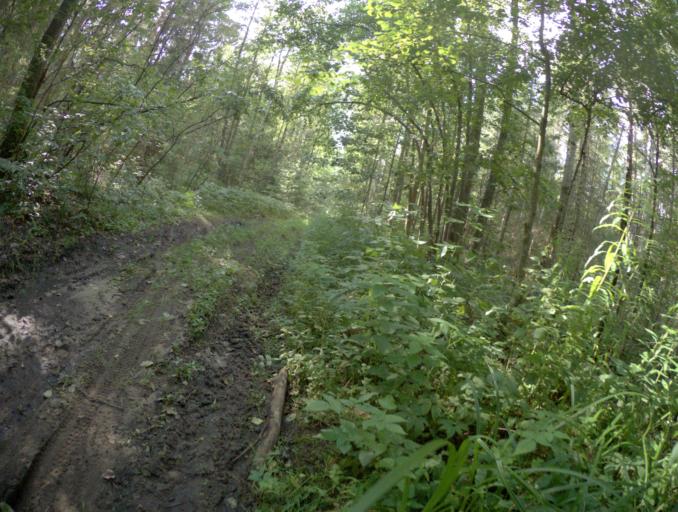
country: RU
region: Vladimir
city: Sobinka
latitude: 55.9103
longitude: 40.1194
